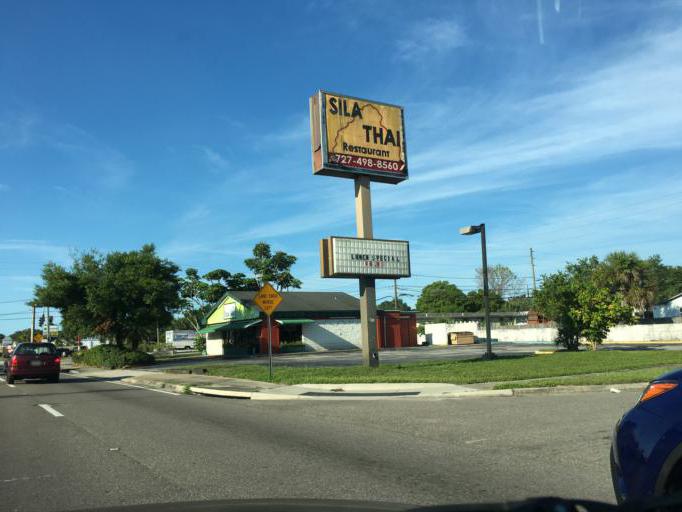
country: US
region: Florida
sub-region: Pinellas County
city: West and East Lealman
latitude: 27.8074
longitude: -82.7001
